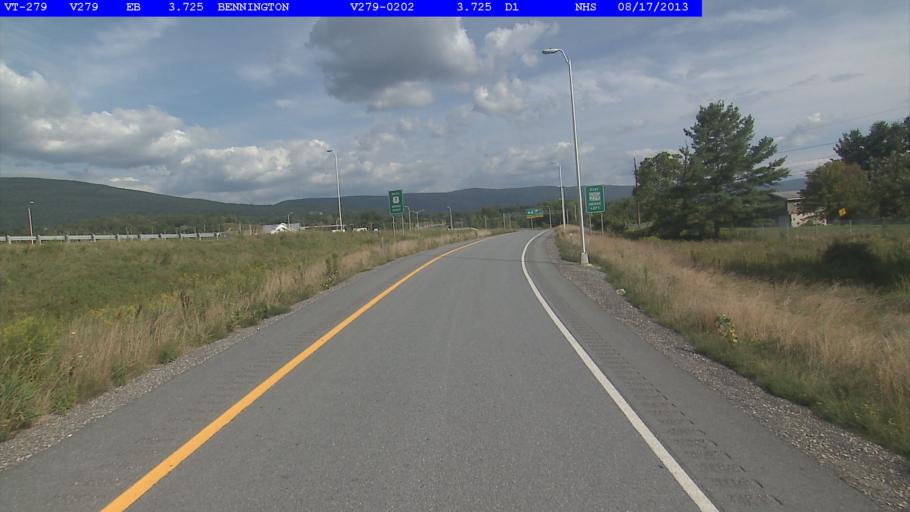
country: US
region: Vermont
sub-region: Bennington County
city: Bennington
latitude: 42.9049
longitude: -73.2086
